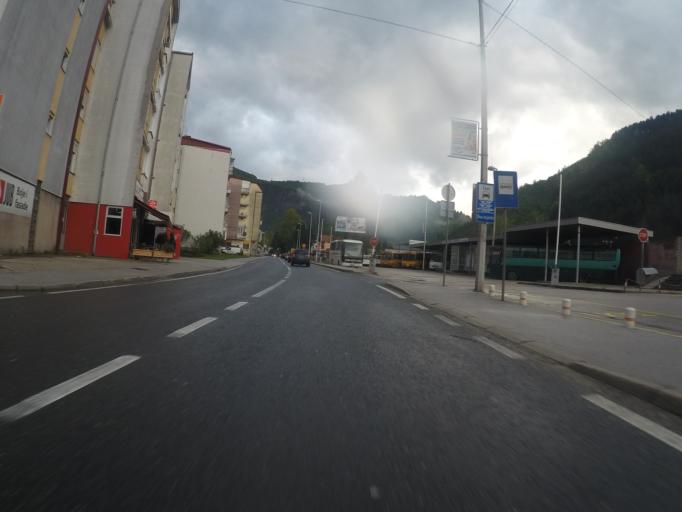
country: BA
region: Federation of Bosnia and Herzegovina
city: Jablanica
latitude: 43.6578
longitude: 17.7620
